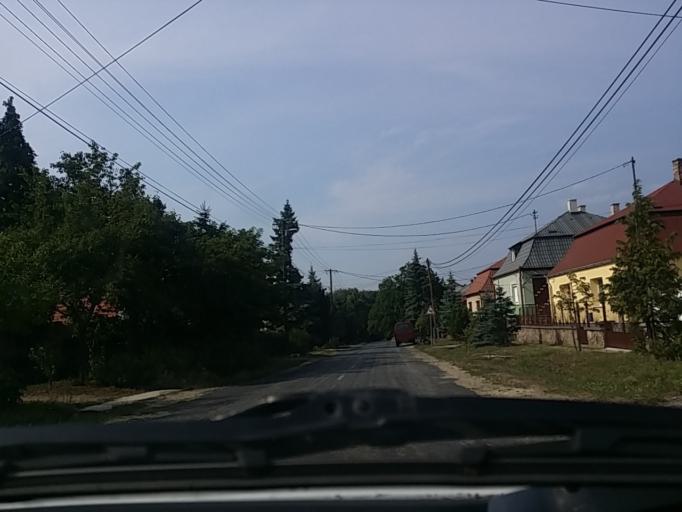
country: HU
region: Komarom-Esztergom
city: Oroszlany
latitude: 47.4770
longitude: 18.3957
